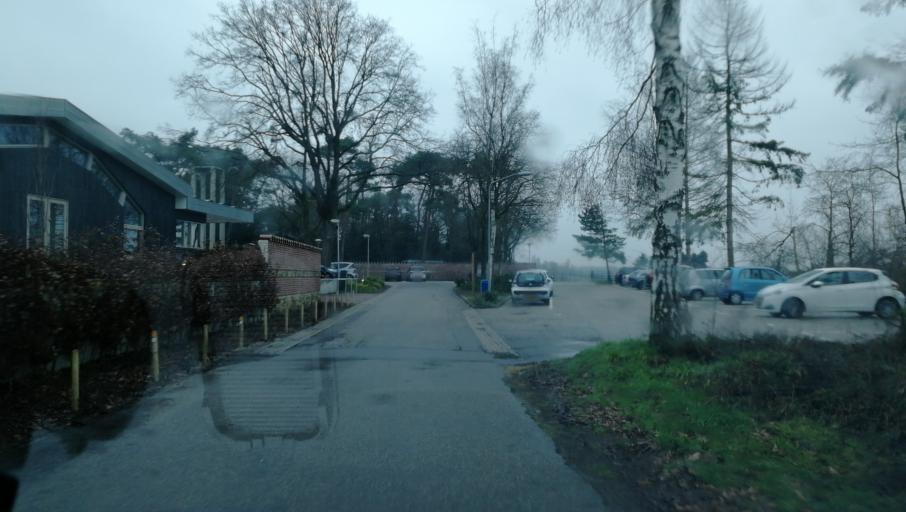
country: NL
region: Limburg
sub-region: Gemeente Venlo
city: Tegelen
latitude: 51.3683
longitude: 6.1091
